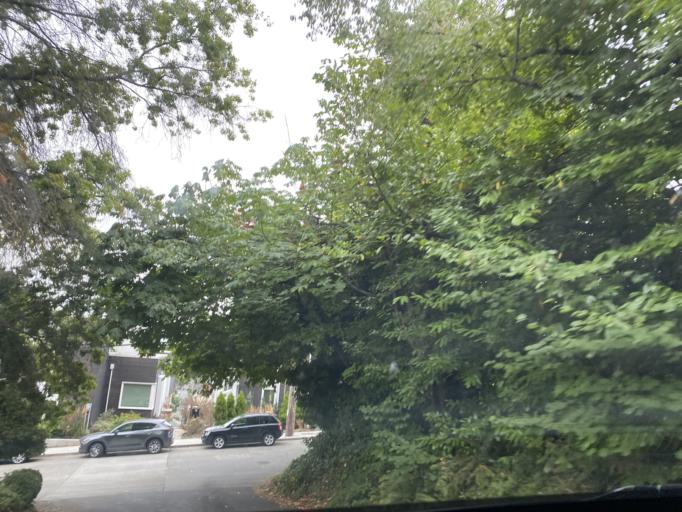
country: US
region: Washington
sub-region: King County
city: Seattle
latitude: 47.6469
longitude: -122.3640
